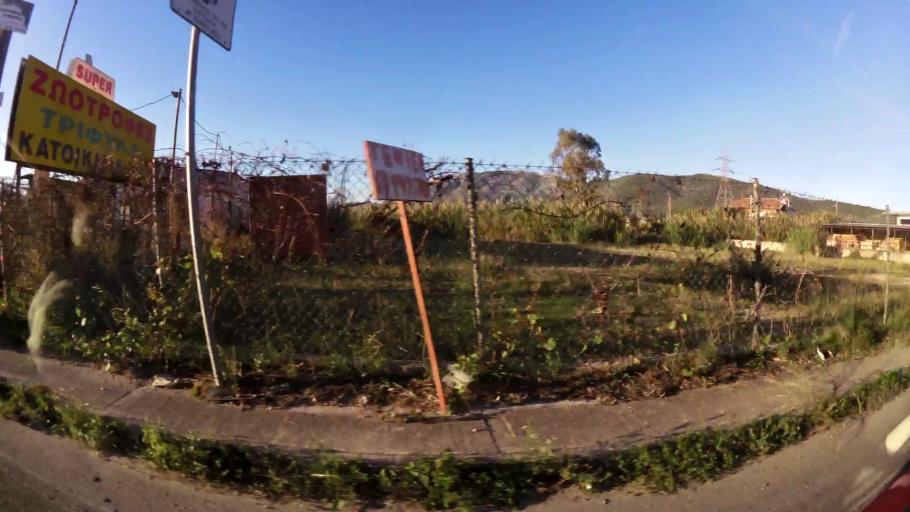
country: GR
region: Attica
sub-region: Nomarchia Anatolikis Attikis
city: Pallini
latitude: 37.9980
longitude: 23.8663
